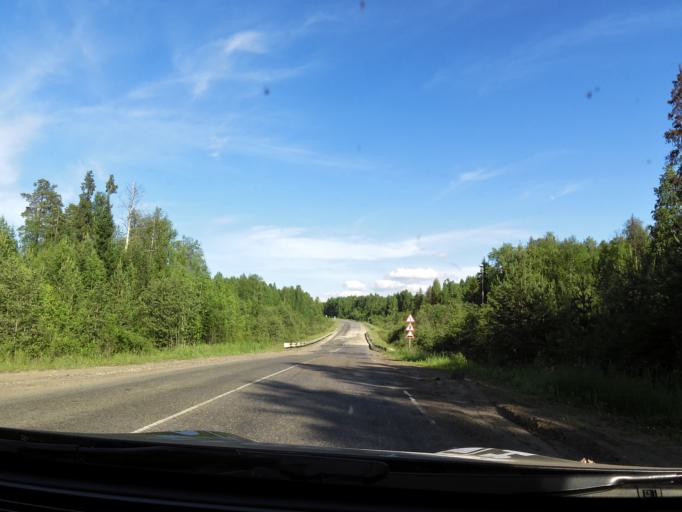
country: RU
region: Kirov
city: Chernaya Kholunitsa
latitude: 58.8930
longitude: 51.3366
